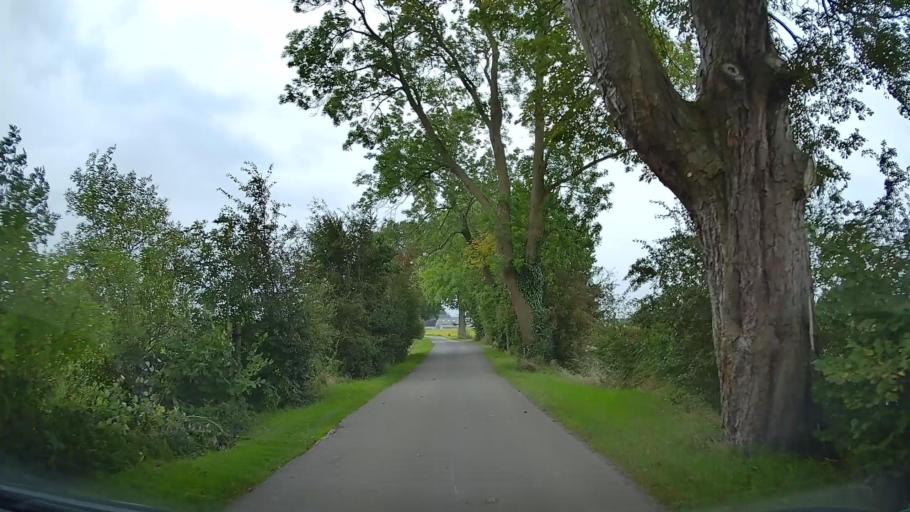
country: DE
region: Schleswig-Holstein
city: Kollmar
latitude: 53.6758
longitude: 9.4888
